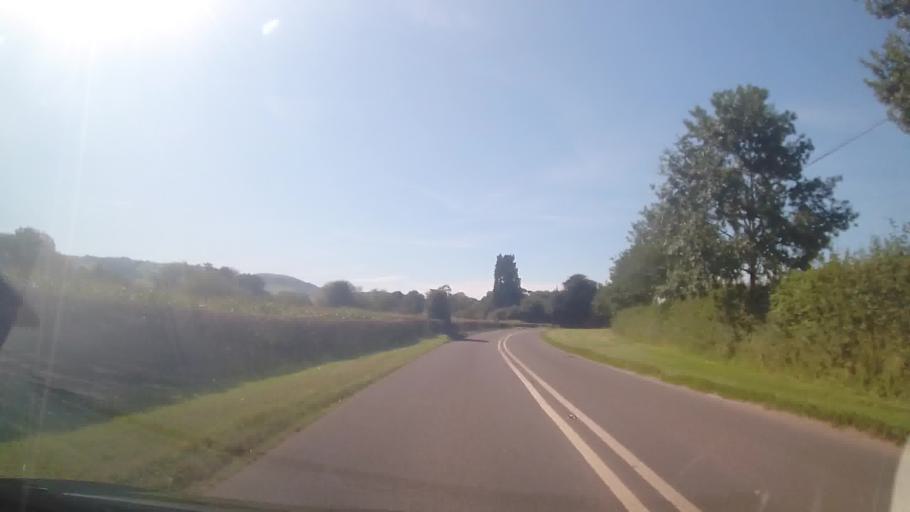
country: GB
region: Wales
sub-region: Sir Powys
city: Montgomery
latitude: 52.5301
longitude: -3.1128
